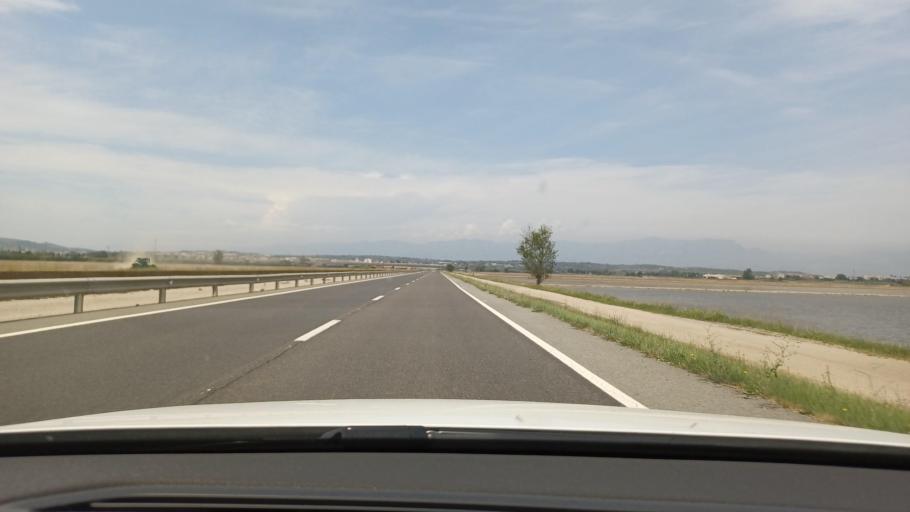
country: ES
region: Catalonia
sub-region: Provincia de Tarragona
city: Amposta
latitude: 40.7123
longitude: 0.6094
